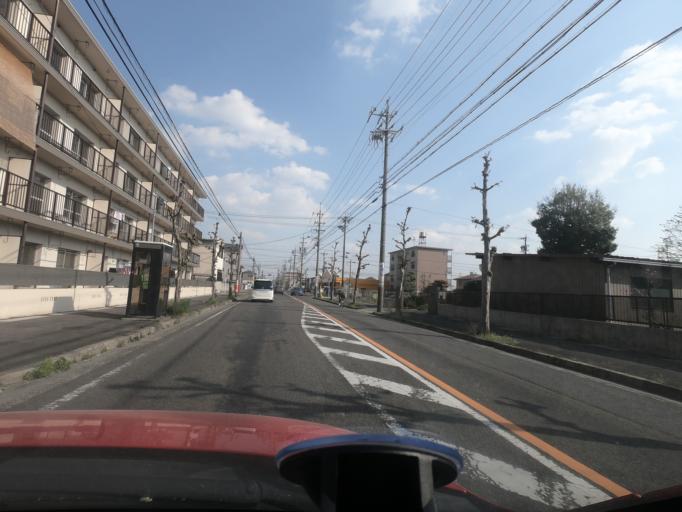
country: JP
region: Aichi
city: Kasugai
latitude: 35.2468
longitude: 136.9619
